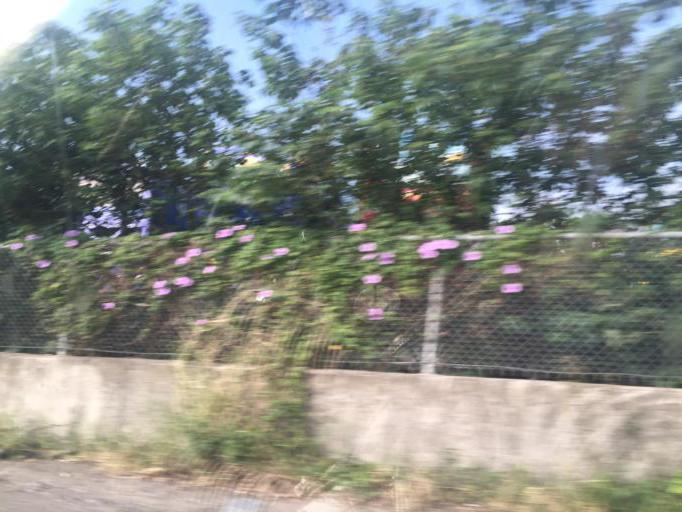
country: TW
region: Taiwan
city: Daxi
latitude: 24.8633
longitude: 121.2228
